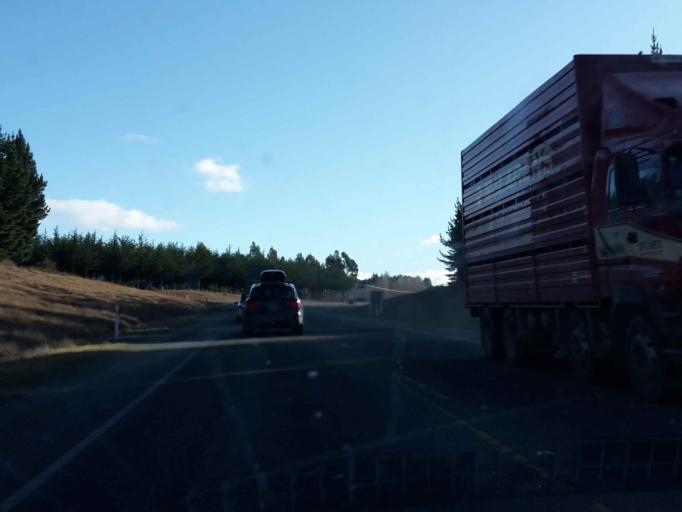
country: NZ
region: Otago
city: Oamaru
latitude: -45.2478
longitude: 170.7913
